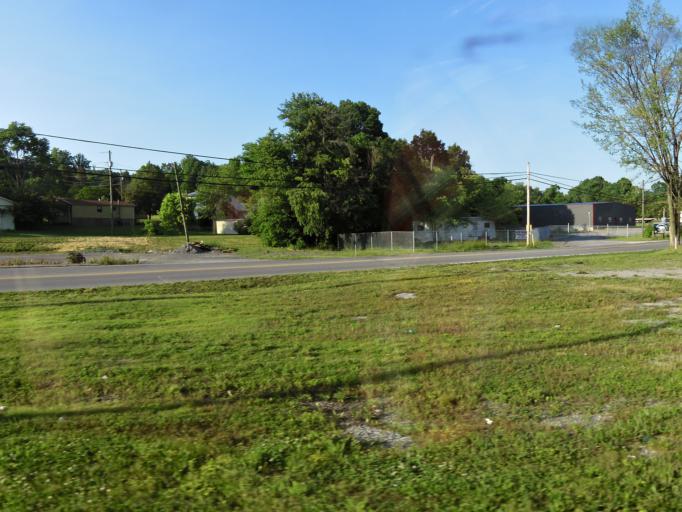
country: US
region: Tennessee
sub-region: Sevier County
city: Seymour
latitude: 35.8839
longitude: -83.7911
